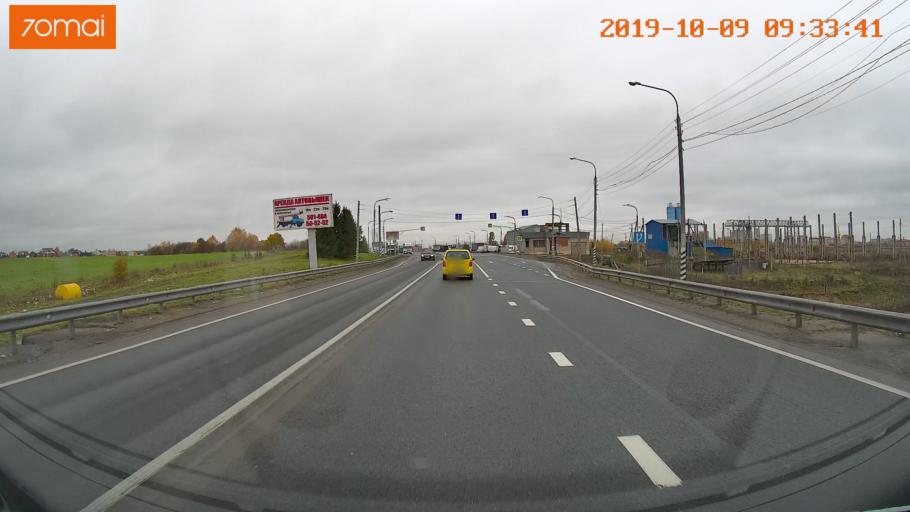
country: RU
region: Vologda
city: Vologda
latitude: 59.1703
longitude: 39.9100
